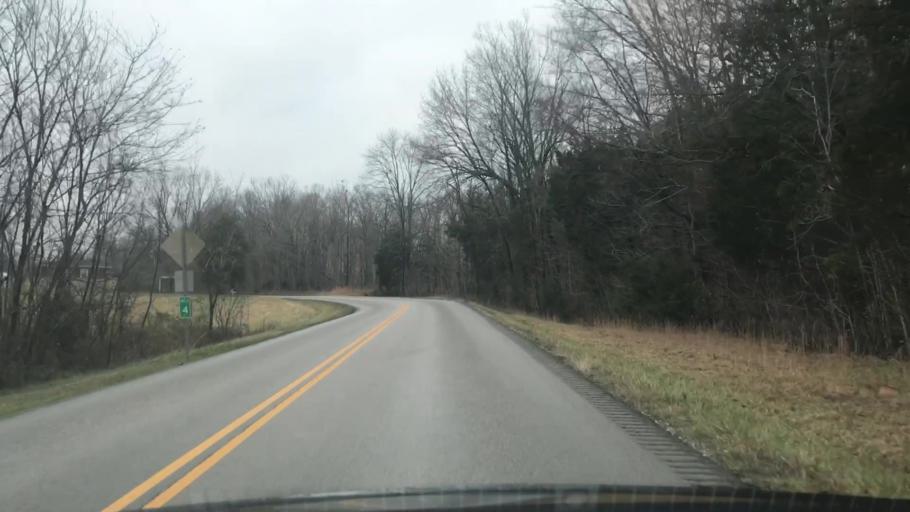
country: US
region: Kentucky
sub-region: Barren County
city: Glasgow
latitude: 36.8845
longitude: -85.7918
